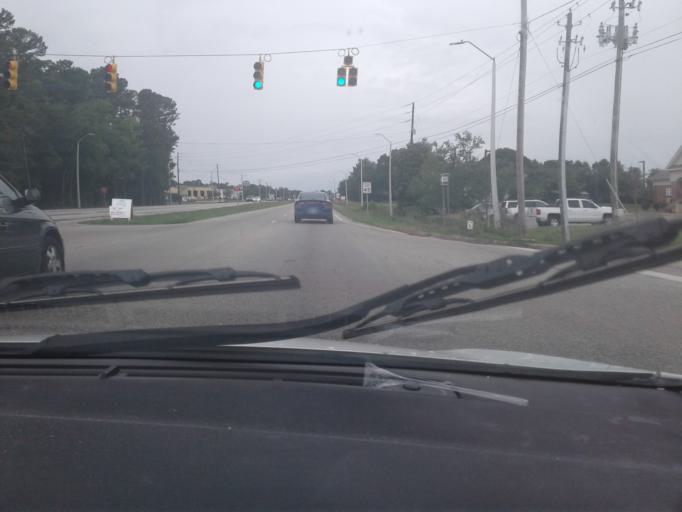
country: US
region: North Carolina
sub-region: Harnett County
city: Erwin
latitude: 35.3242
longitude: -78.6473
